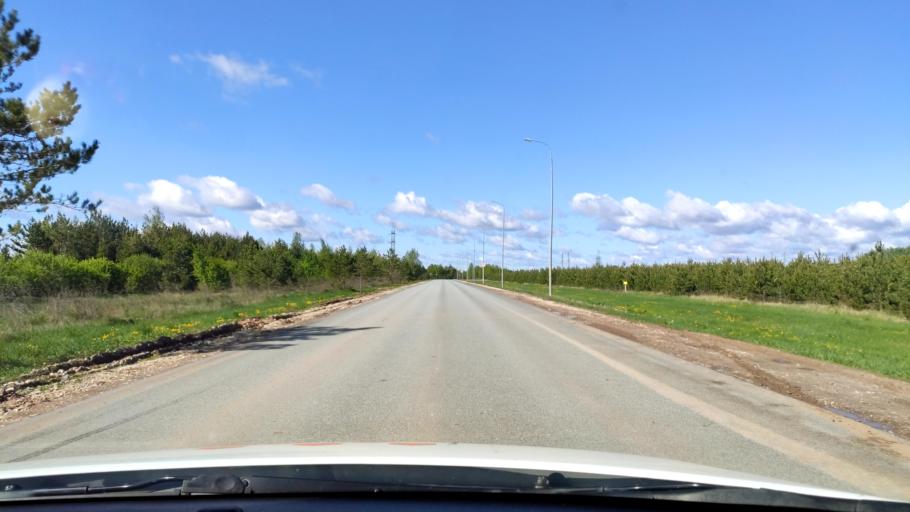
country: RU
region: Tatarstan
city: Sviyazhsk
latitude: 55.7266
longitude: 48.7552
